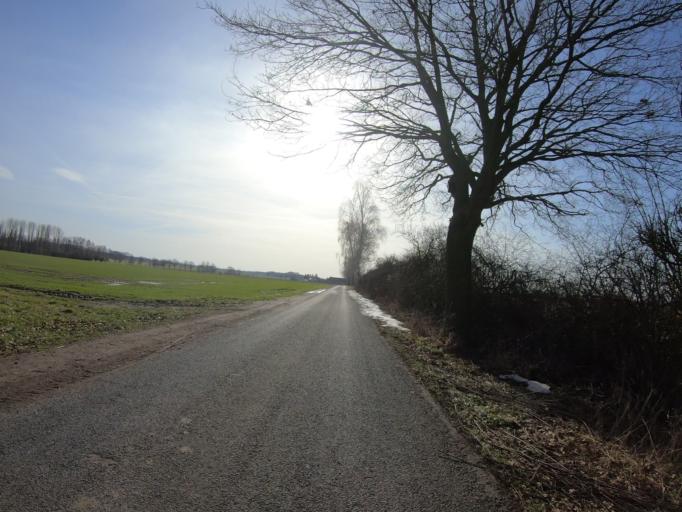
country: DE
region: Lower Saxony
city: Isenbuttel
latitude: 52.4150
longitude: 10.5646
